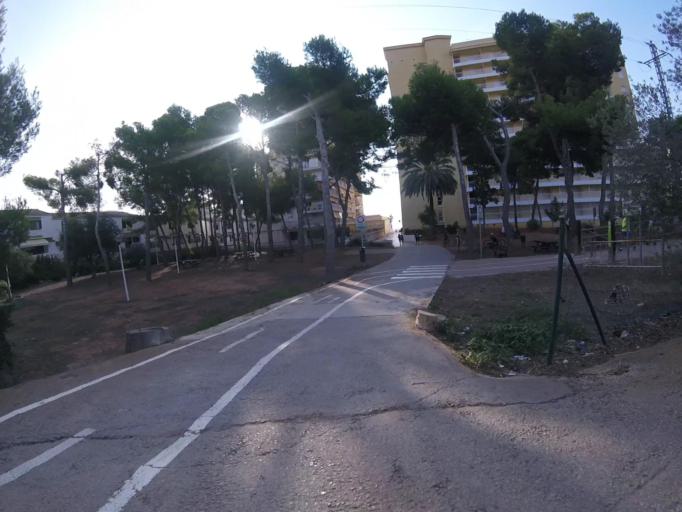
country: ES
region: Valencia
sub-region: Provincia de Castello
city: Orpesa/Oropesa del Mar
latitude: 40.0833
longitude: 0.1370
